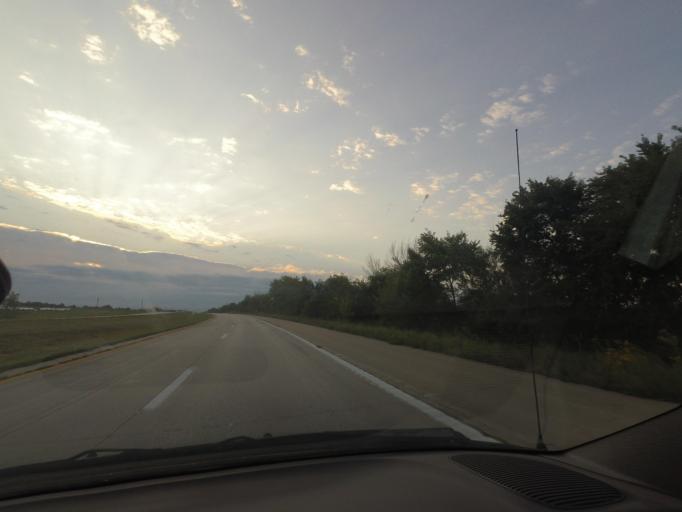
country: US
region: Missouri
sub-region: Shelby County
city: Shelbina
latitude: 39.7402
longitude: -92.2392
